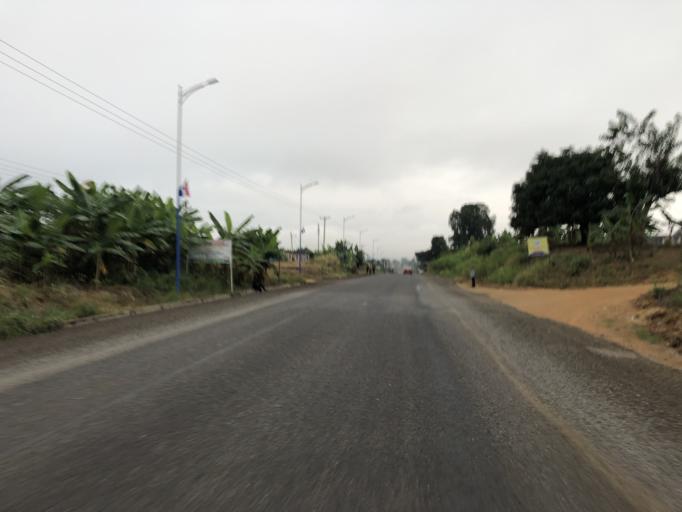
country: GH
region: Eastern
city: Koforidua
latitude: 6.1951
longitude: -0.3609
